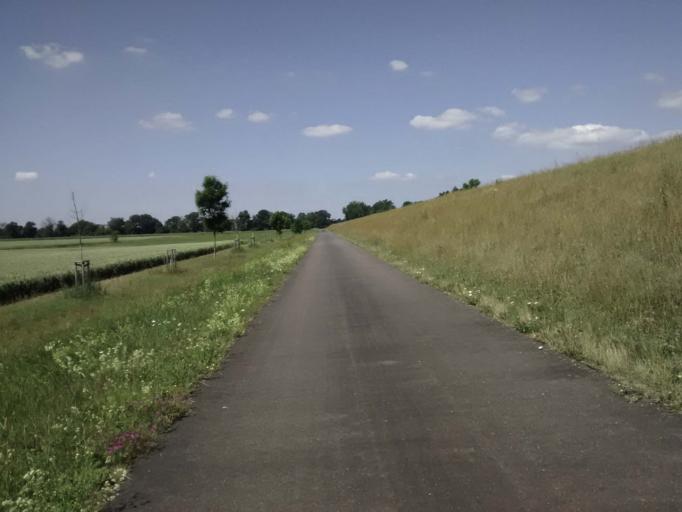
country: DE
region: Saxony-Anhalt
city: Worlitz
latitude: 51.8407
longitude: 12.4683
